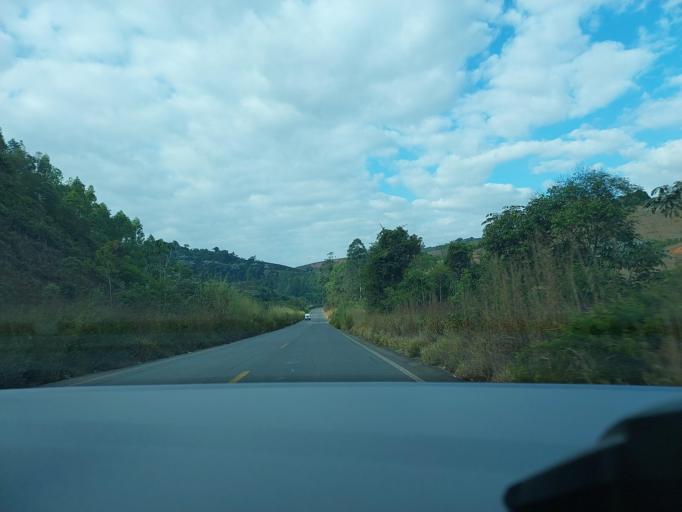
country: BR
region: Minas Gerais
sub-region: Vicosa
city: Vicosa
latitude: -20.8376
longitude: -42.6967
